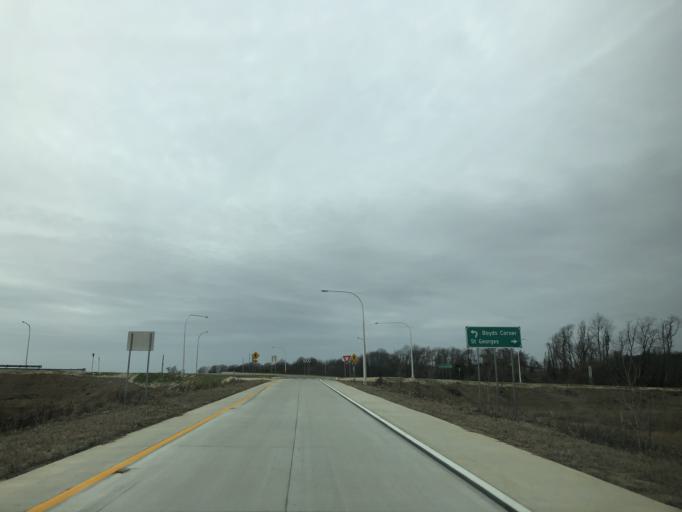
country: US
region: Delaware
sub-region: New Castle County
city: Middletown
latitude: 39.5252
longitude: -75.6785
